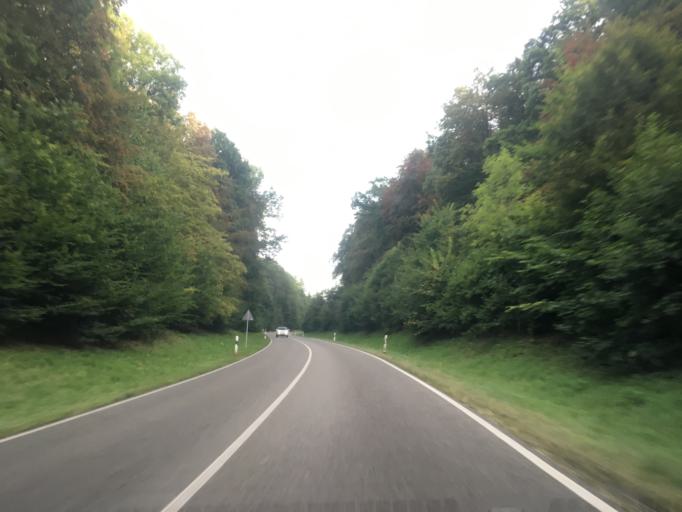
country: DE
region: Baden-Wuerttemberg
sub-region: Tuebingen Region
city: Eningen unter Achalm
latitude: 48.5103
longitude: 9.2642
